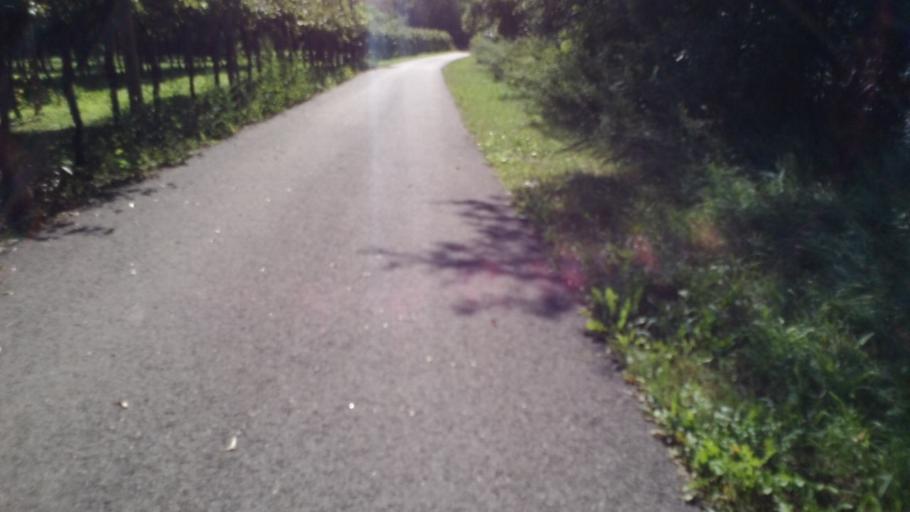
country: IT
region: Veneto
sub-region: Provincia di Verona
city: Brentino Belluno
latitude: 45.6668
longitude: 10.9028
